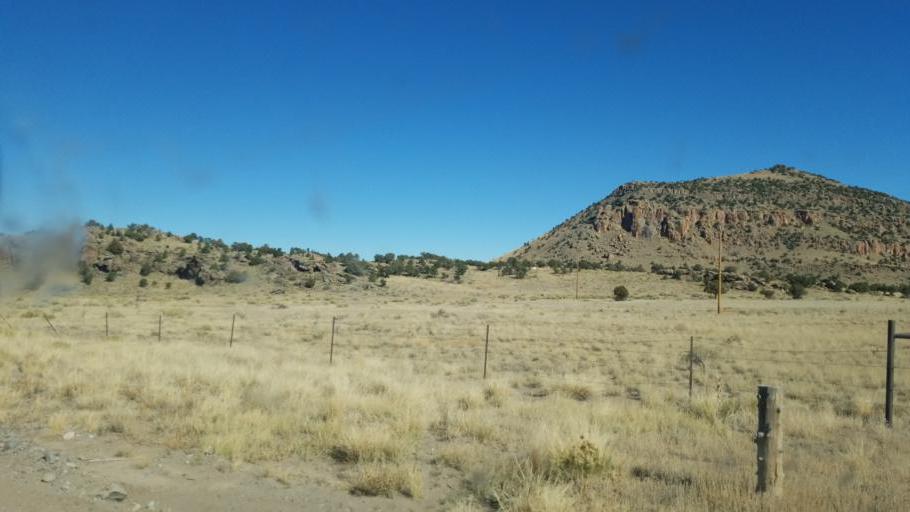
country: US
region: Colorado
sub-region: Rio Grande County
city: Del Norte
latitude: 37.6292
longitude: -106.3630
